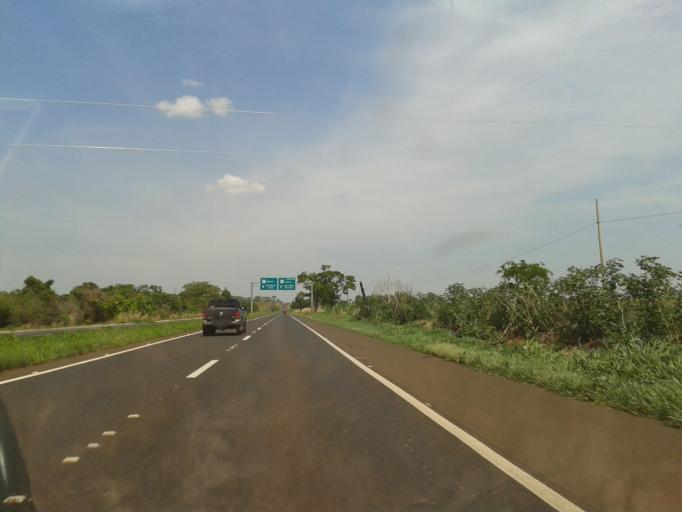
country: BR
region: Minas Gerais
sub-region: Monte Alegre De Minas
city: Monte Alegre de Minas
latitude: -18.8671
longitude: -48.7605
